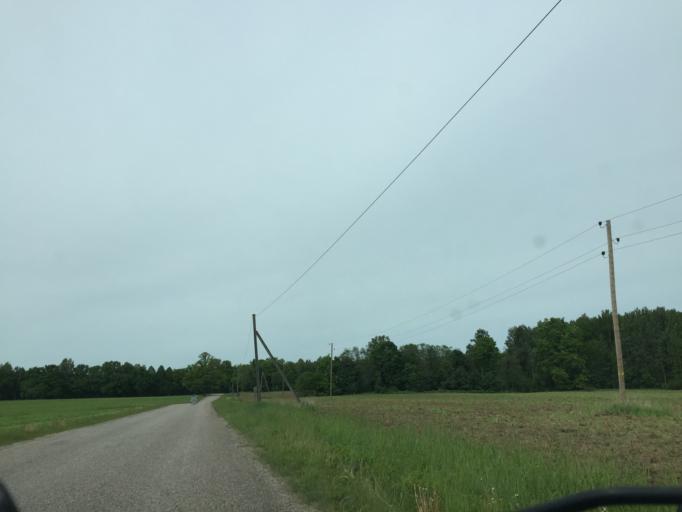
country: LV
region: Koceni
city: Koceni
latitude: 57.4802
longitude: 25.3645
